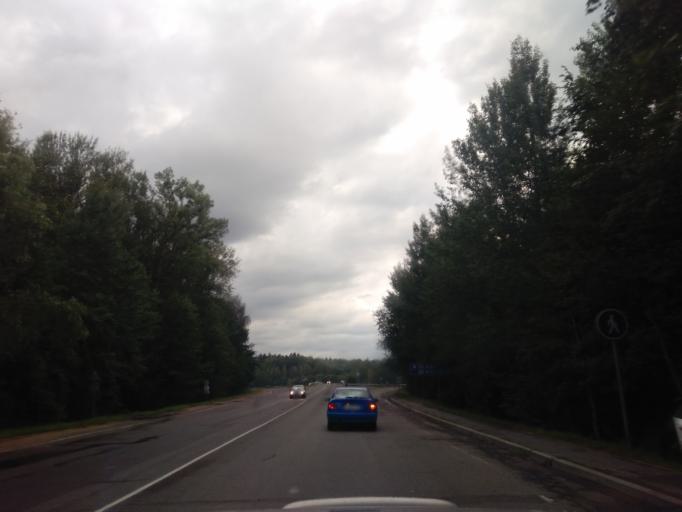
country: BY
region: Minsk
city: Enyerhyetykaw
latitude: 53.5897
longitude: 27.0444
